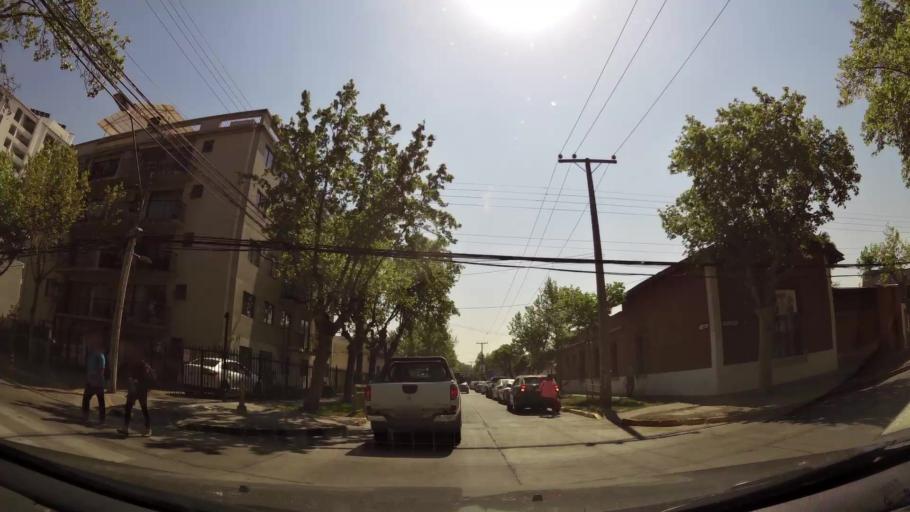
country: CL
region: Santiago Metropolitan
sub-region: Provincia de Maipo
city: San Bernardo
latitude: -33.5921
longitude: -70.7081
